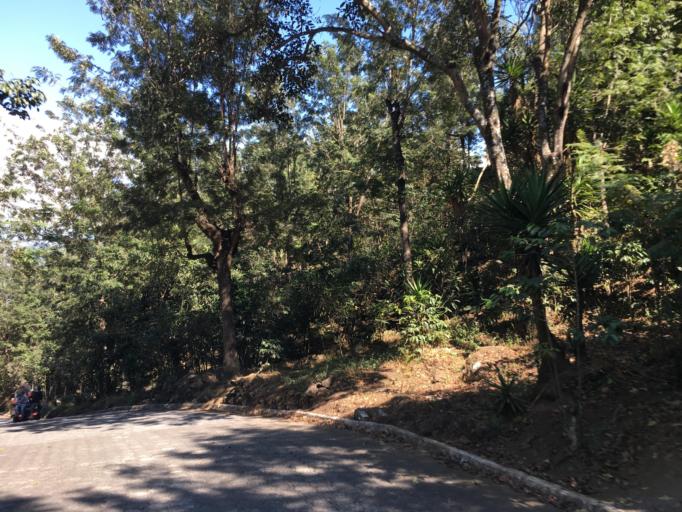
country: GT
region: Solola
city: Santiago Atitlan
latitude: 14.6657
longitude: -91.1721
